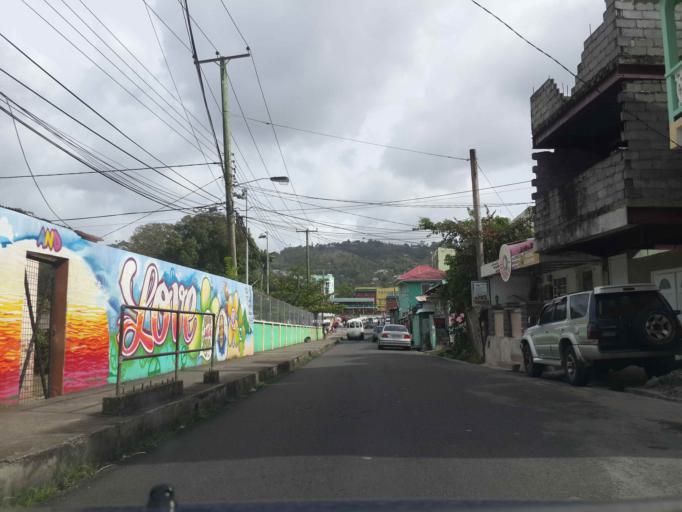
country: LC
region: Castries Quarter
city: Bisee
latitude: 14.0135
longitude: -60.9879
